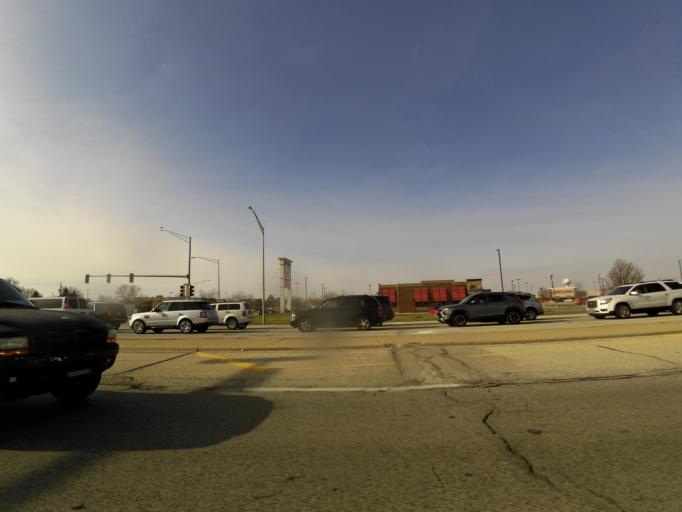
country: US
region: Illinois
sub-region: Macon County
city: Forsyth
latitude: 39.9179
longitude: -88.9554
